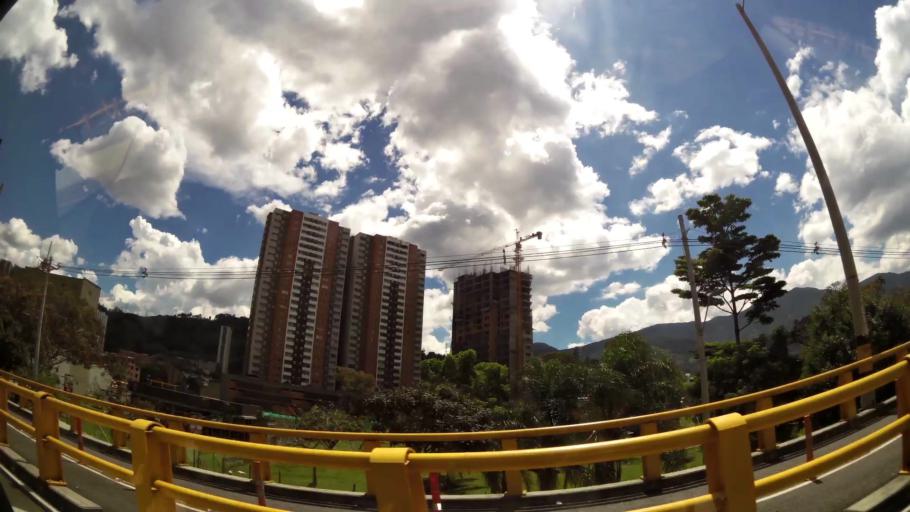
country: CO
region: Antioquia
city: Sabaneta
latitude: 6.1513
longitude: -75.6240
